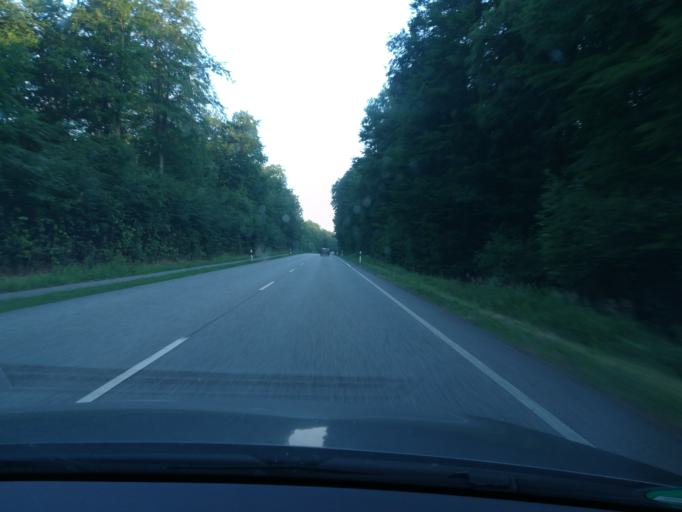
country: DE
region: Schleswig-Holstein
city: Brunstorf
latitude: 53.5263
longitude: 10.4423
